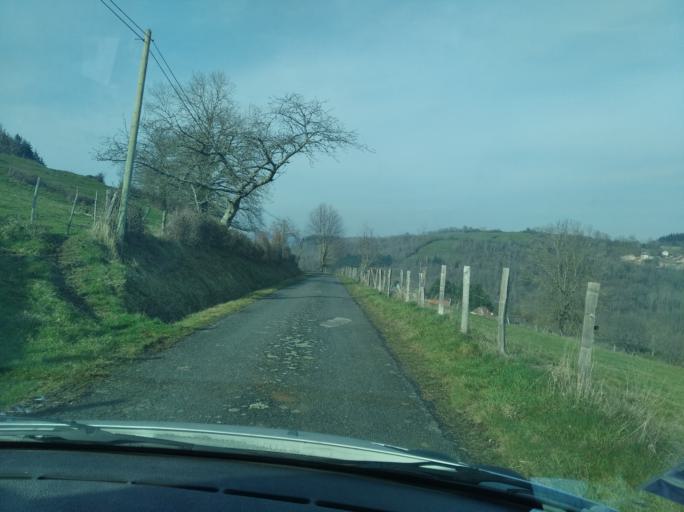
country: FR
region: Rhone-Alpes
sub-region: Departement de la Loire
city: La Pacaudiere
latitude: 46.1657
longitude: 3.7544
